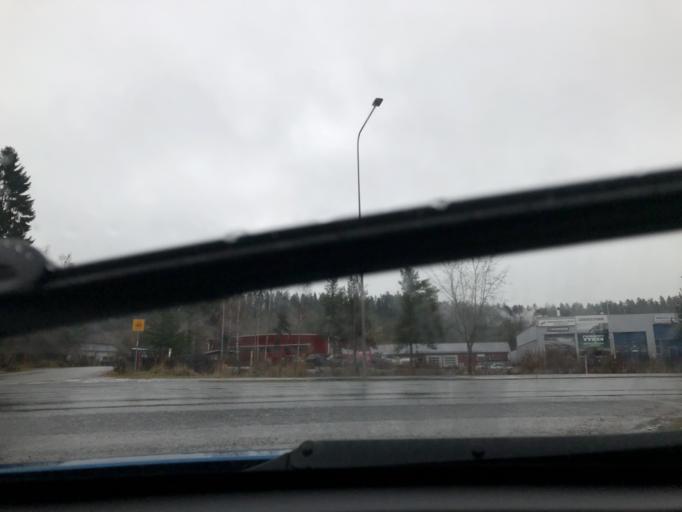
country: FI
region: Pirkanmaa
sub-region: Tampere
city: Kangasala
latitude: 61.4713
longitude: 24.0299
